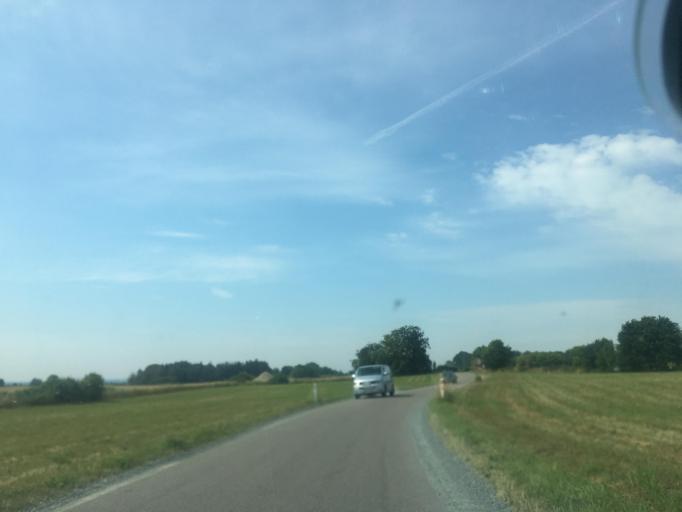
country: DK
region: Zealand
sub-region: Faxe Kommune
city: Fakse
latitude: 55.1825
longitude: 12.0945
